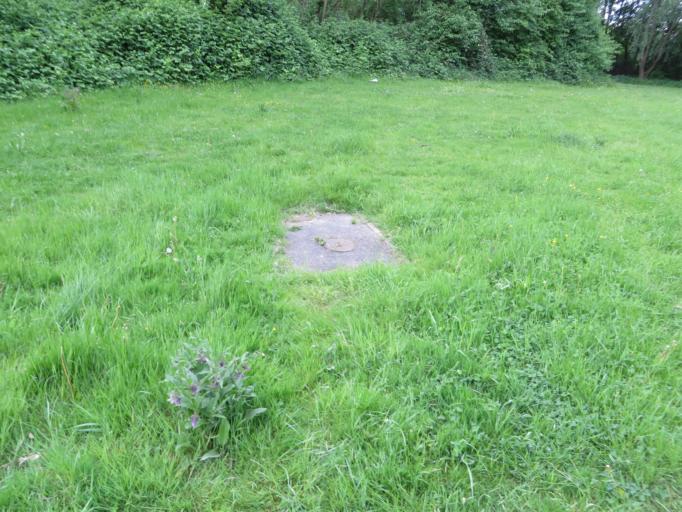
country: DE
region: North Rhine-Westphalia
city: Witten
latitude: 51.4551
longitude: 7.3187
